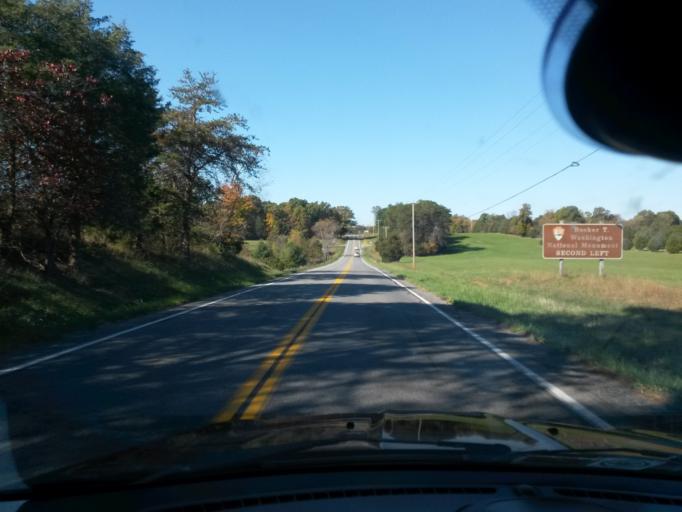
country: US
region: Virginia
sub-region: Franklin County
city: North Shore
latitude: 37.1209
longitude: -79.7284
